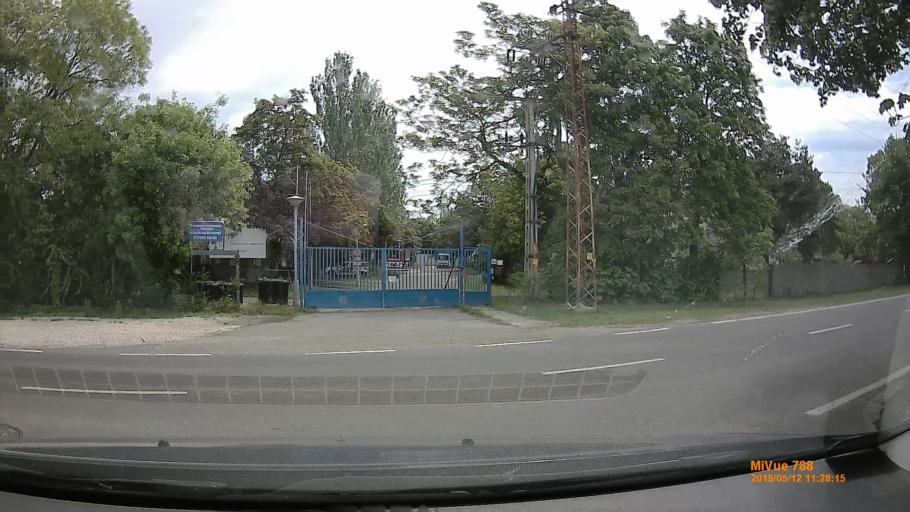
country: HU
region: Budapest
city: Budapest XVII. keruelet
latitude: 47.4643
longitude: 19.2471
